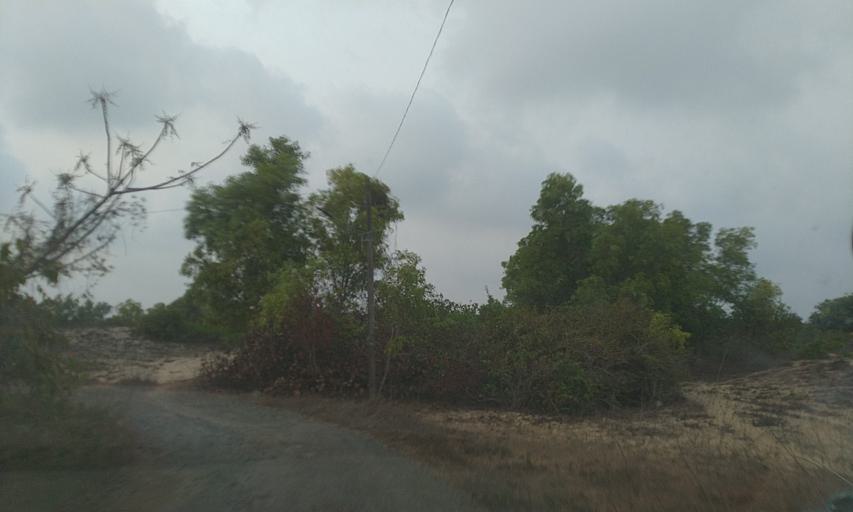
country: IN
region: Goa
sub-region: South Goa
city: Cavelossim
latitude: 15.1858
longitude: 73.9437
